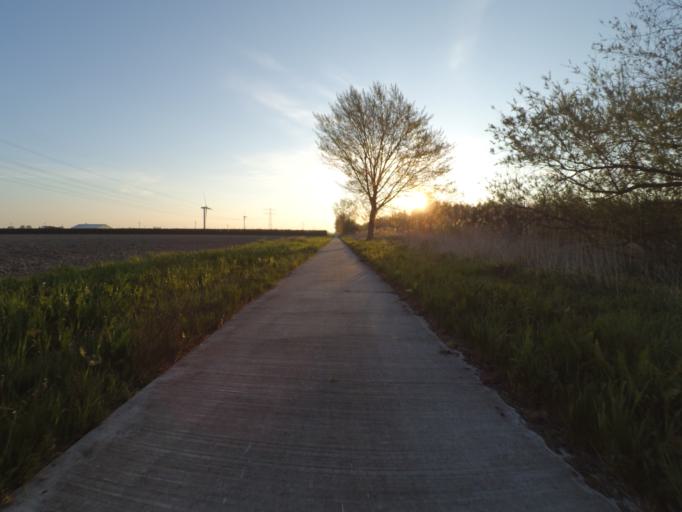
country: NL
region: Flevoland
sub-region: Gemeente Zeewolde
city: Zeewolde
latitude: 52.3505
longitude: 5.4754
